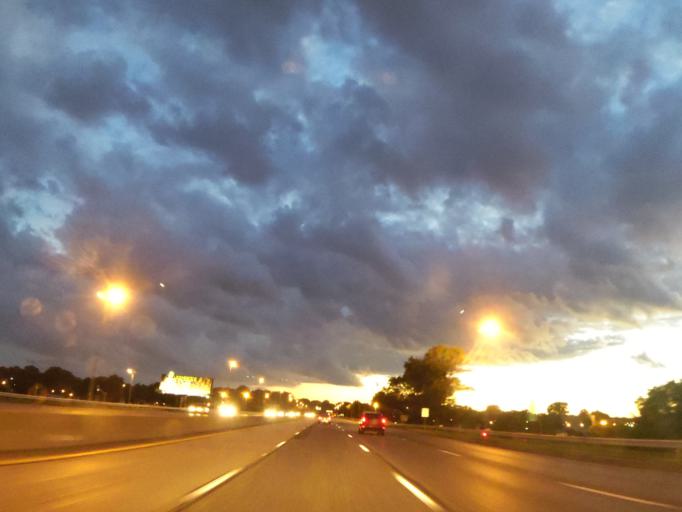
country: US
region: Missouri
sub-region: Saint Louis County
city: Lemay
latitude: 38.5534
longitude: -90.2686
